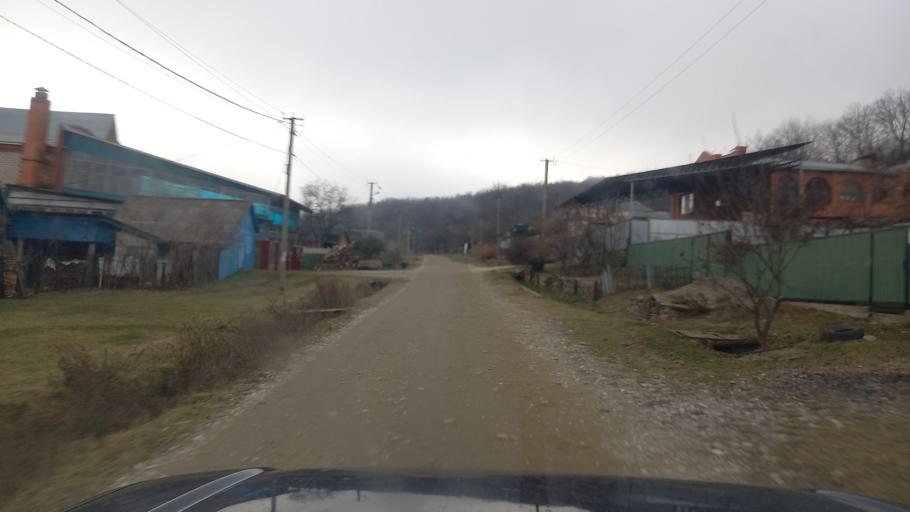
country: RU
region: Krasnodarskiy
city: Neftegorsk
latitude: 44.2467
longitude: 39.7542
